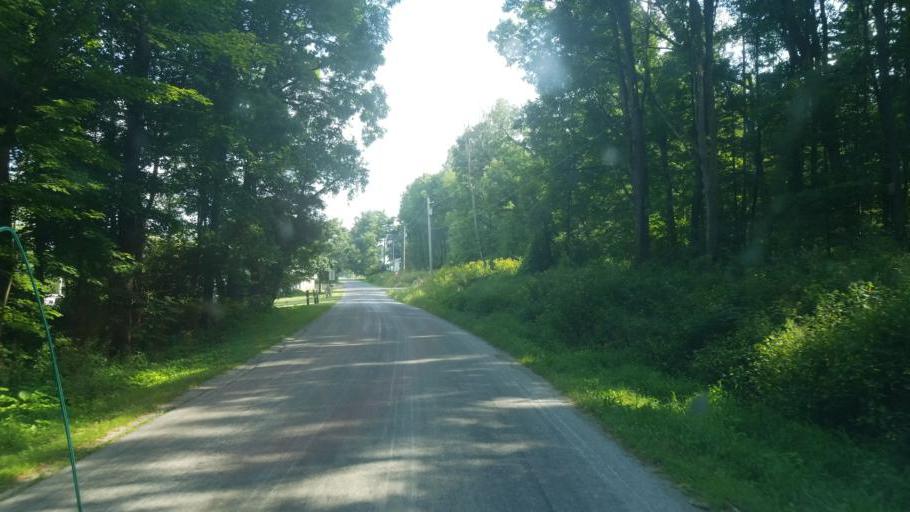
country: US
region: Ohio
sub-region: Wayne County
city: West Salem
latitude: 40.9535
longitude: -82.0342
